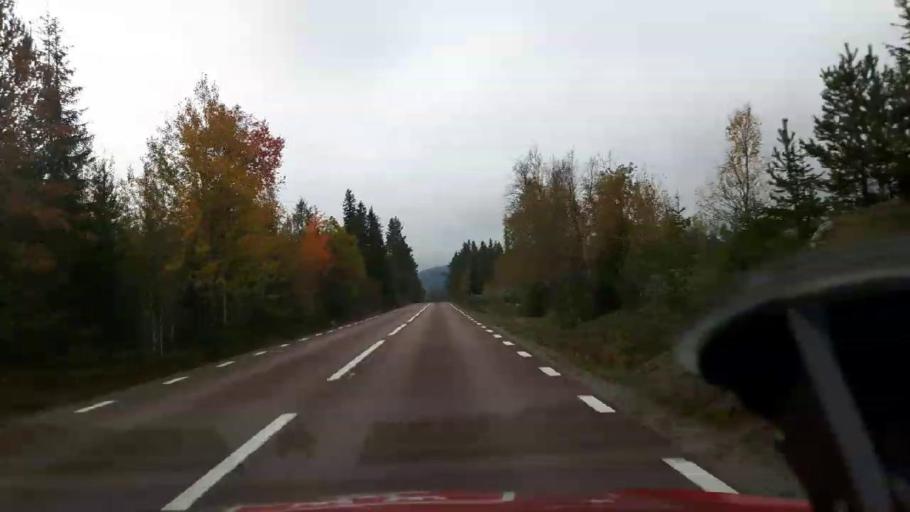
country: SE
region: Jaemtland
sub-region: Harjedalens Kommun
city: Sveg
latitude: 62.3203
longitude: 14.7450
